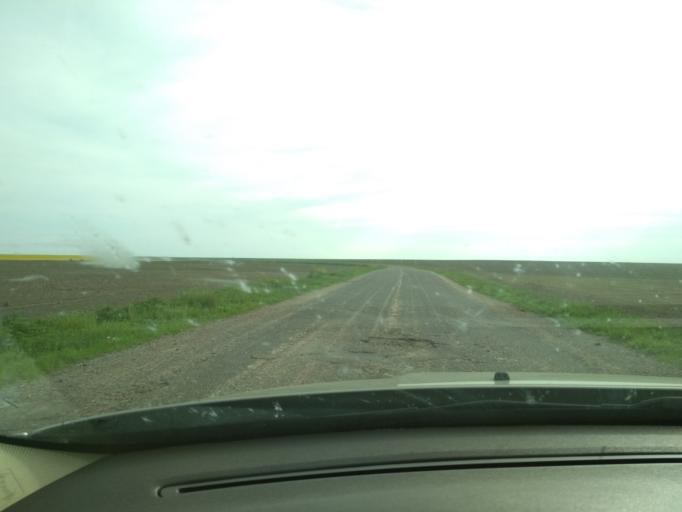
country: BY
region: Grodnenskaya
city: Mir
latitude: 53.4189
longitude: 26.4297
